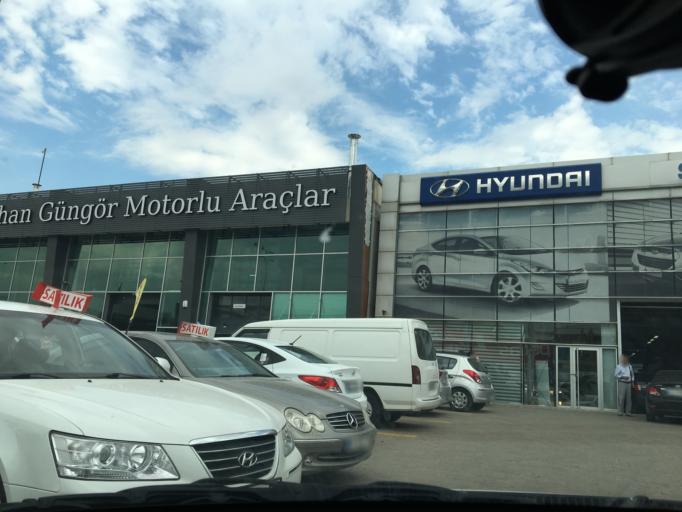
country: TR
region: Ankara
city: Batikent
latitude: 39.9345
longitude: 32.7126
